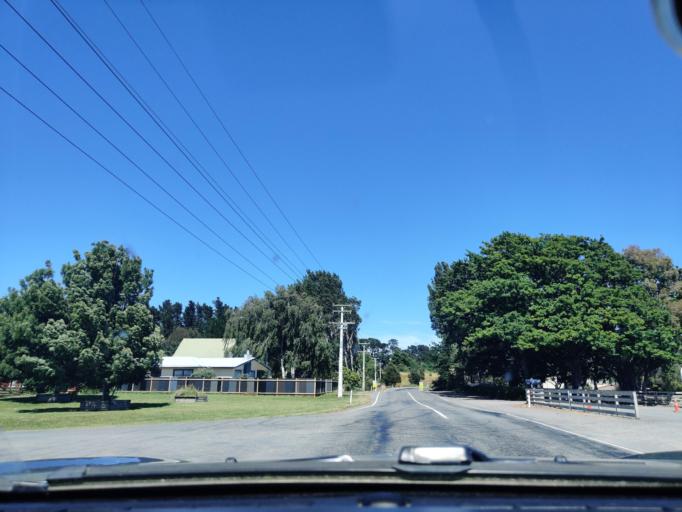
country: NZ
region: Wellington
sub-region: South Wairarapa District
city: Waipawa
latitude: -41.2274
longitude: 175.3423
